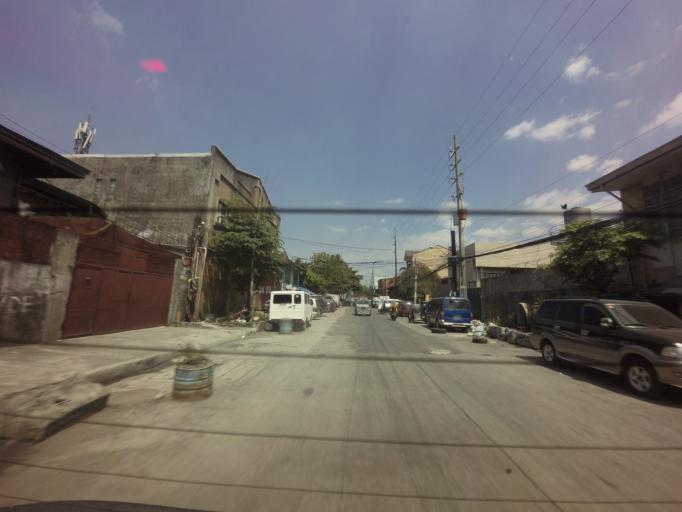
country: PH
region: Metro Manila
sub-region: Caloocan City
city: Niugan
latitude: 14.6334
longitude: 120.9652
